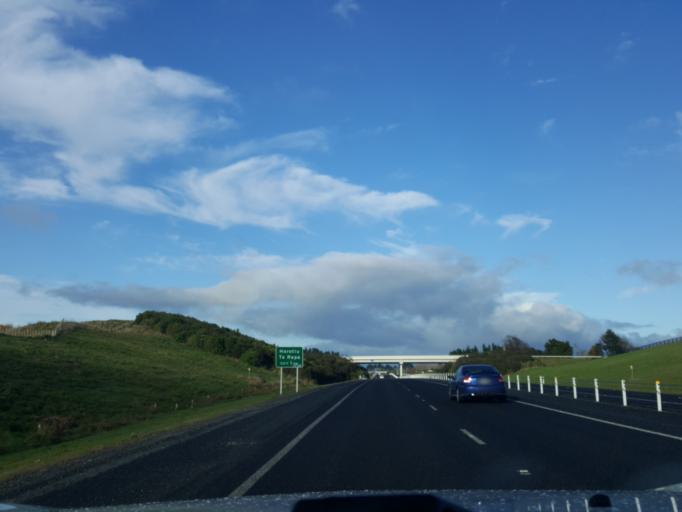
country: NZ
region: Waikato
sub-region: Waikato District
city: Ngaruawahia
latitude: -37.6946
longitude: 175.2130
